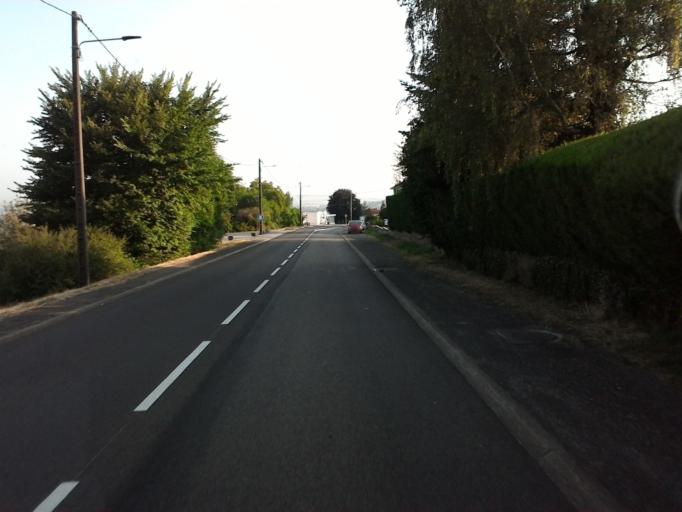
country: FR
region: Franche-Comte
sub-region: Departement de la Haute-Saone
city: Echenoz-la-Meline
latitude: 47.6021
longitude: 6.1413
